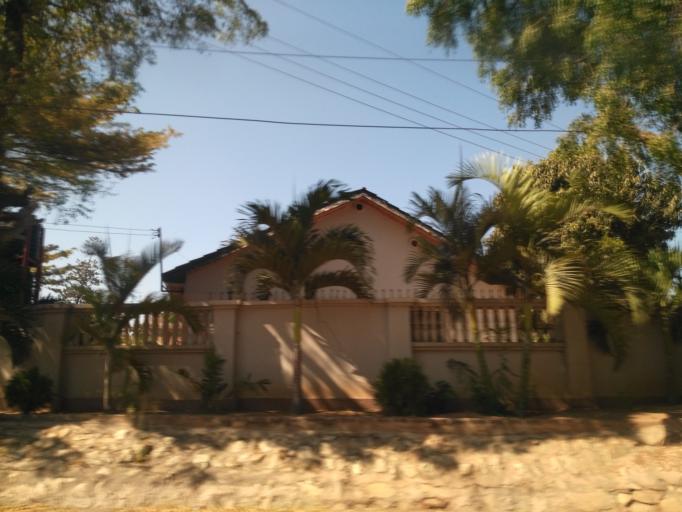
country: TZ
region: Dodoma
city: Dodoma
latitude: -6.1679
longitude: 35.7513
